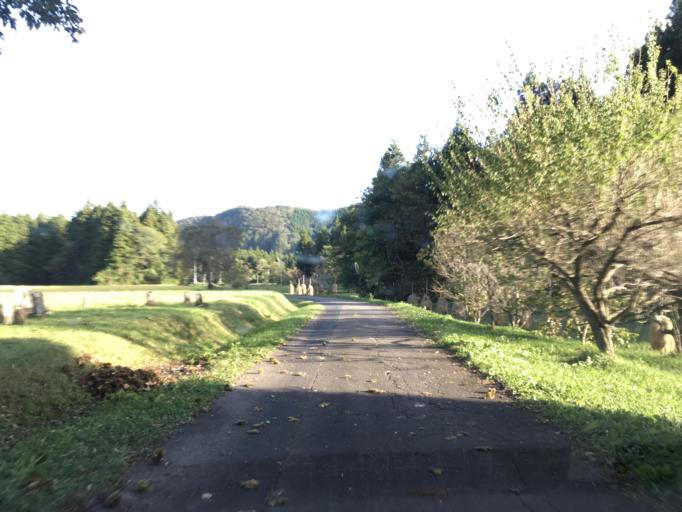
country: JP
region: Iwate
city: Ichinoseki
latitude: 38.9749
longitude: 140.9538
